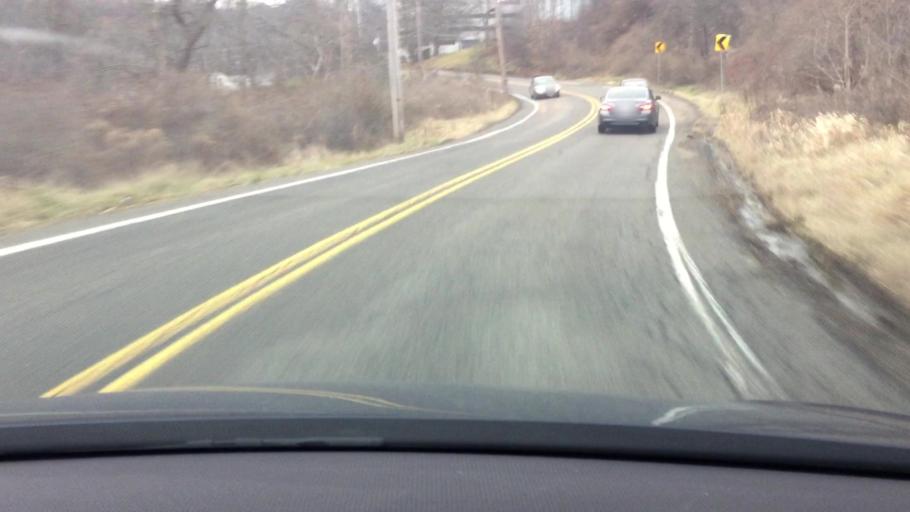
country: US
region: Pennsylvania
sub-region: Allegheny County
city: Rennerdale
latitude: 40.4382
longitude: -80.1420
